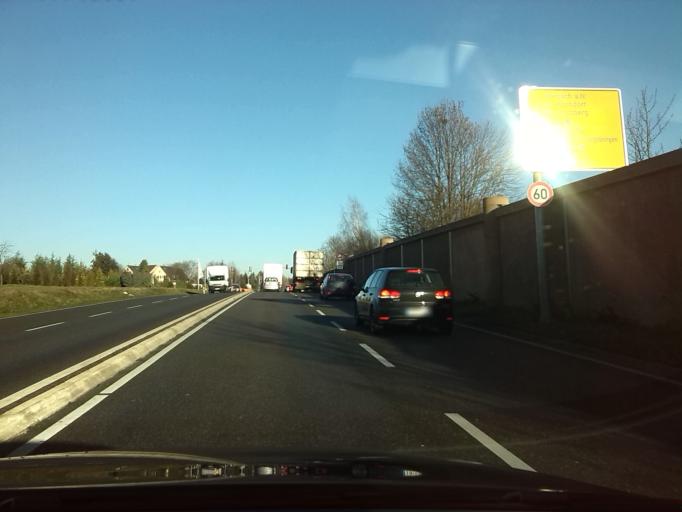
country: DE
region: Baden-Wuerttemberg
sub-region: Regierungsbezirk Stuttgart
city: Stuttgart Muehlhausen
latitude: 48.8774
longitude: 9.2687
